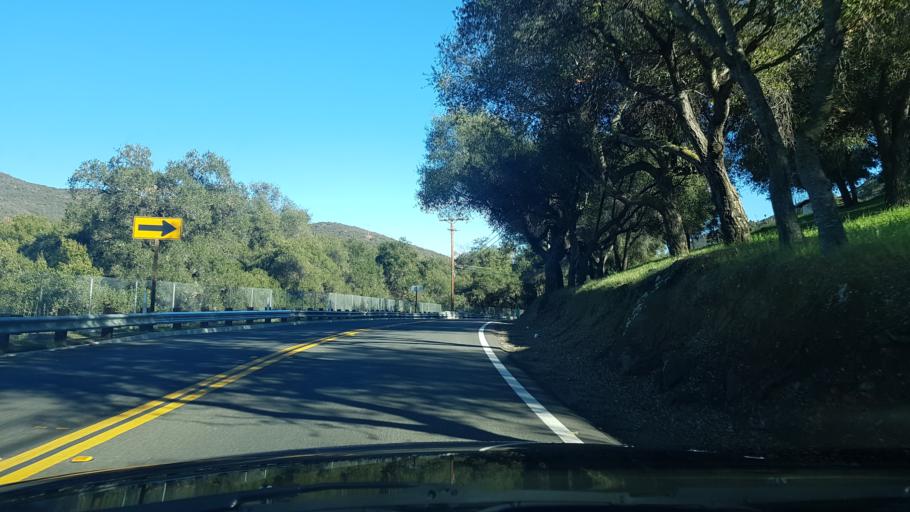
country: US
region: California
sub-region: San Diego County
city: Valley Center
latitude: 33.2055
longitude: -117.0104
